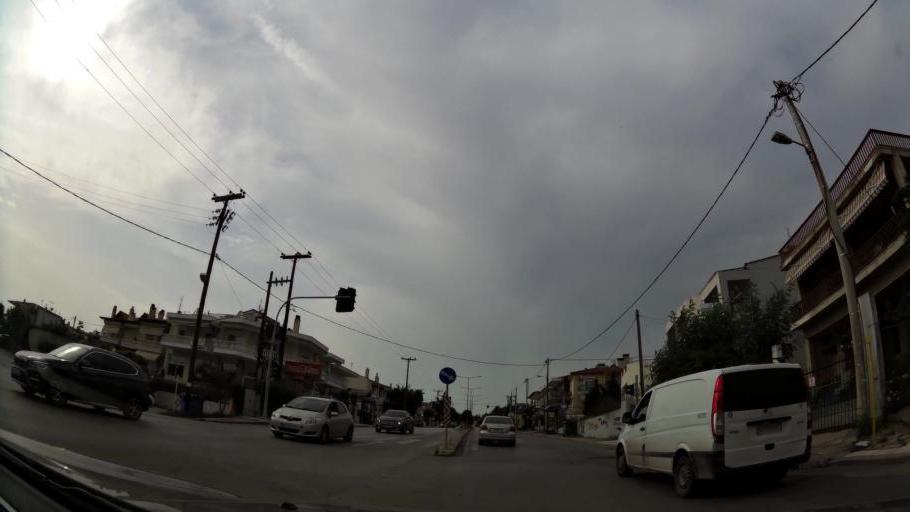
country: GR
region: Central Macedonia
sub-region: Nomos Thessalonikis
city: Oraiokastro
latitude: 40.7220
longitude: 22.9251
